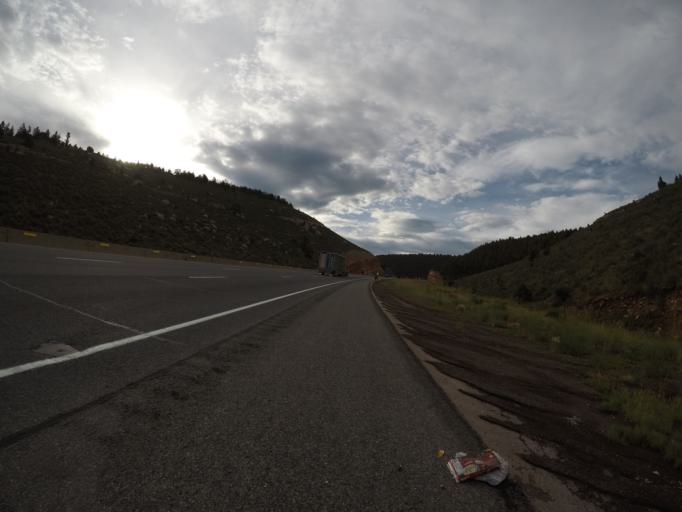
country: US
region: Wyoming
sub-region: Albany County
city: Laramie
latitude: 41.2715
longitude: -105.4823
